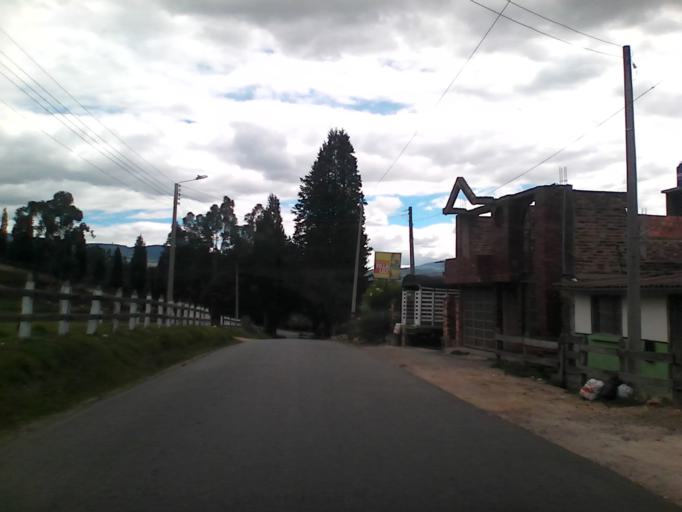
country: CO
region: Boyaca
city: Duitama
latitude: 5.7999
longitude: -73.0619
